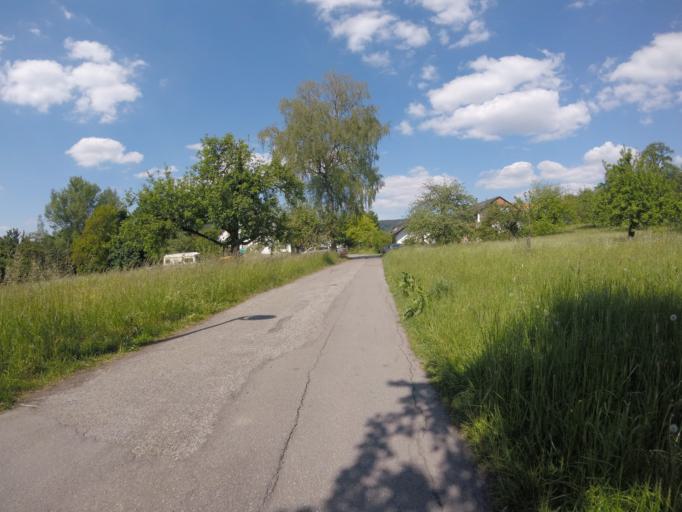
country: DE
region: Baden-Wuerttemberg
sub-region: Regierungsbezirk Stuttgart
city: Sulzbach an der Murr
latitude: 48.9503
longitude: 9.5026
